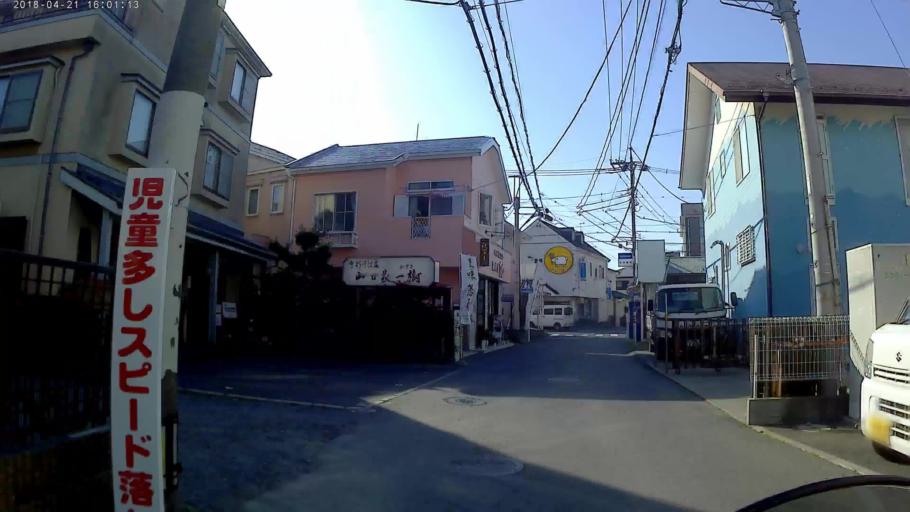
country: JP
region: Kanagawa
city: Fujisawa
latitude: 35.3394
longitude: 139.4399
